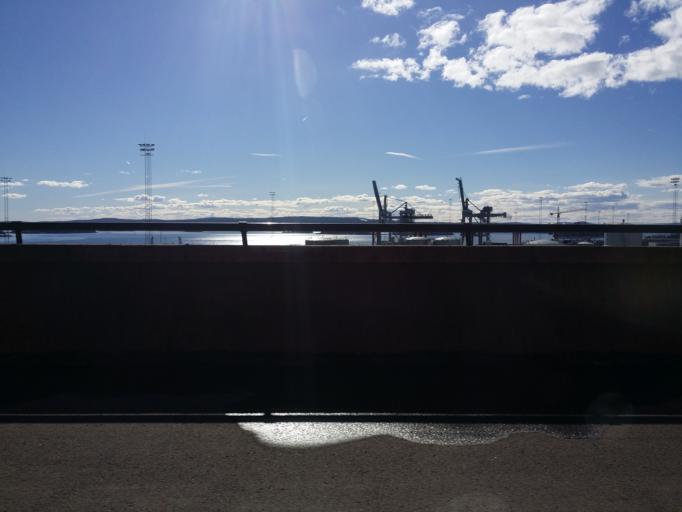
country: NO
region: Oslo
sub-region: Oslo
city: Oslo
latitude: 59.8897
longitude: 10.7637
